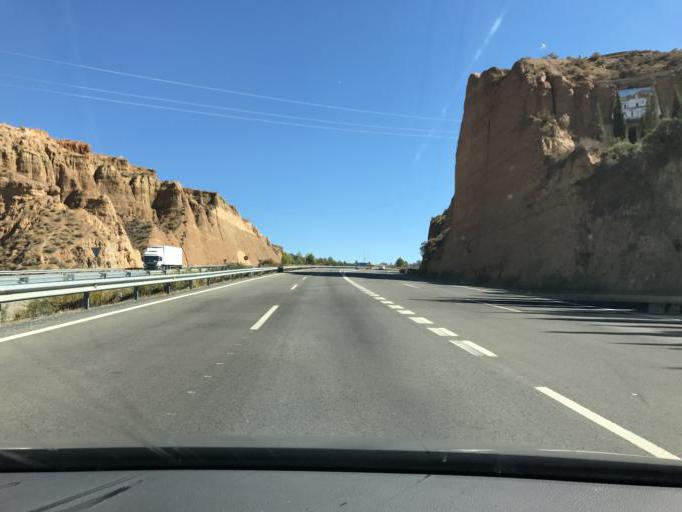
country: ES
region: Andalusia
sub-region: Provincia de Granada
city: Guadix
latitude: 37.3202
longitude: -3.1238
